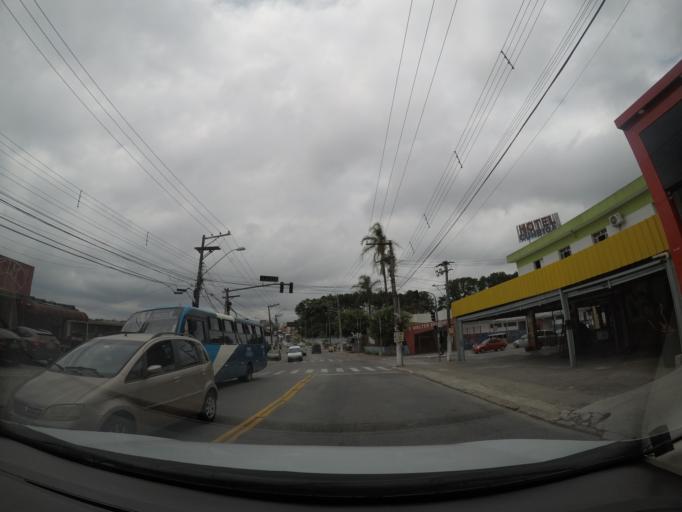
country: BR
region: Sao Paulo
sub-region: Itaquaquecetuba
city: Itaquaquecetuba
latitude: -23.4587
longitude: -46.4108
